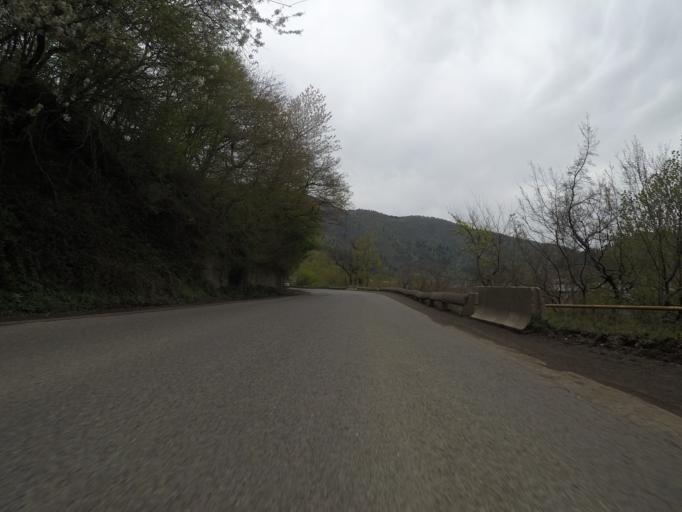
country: GE
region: Samtskhe-Javakheti
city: Borjomi
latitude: 41.9249
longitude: 43.4848
